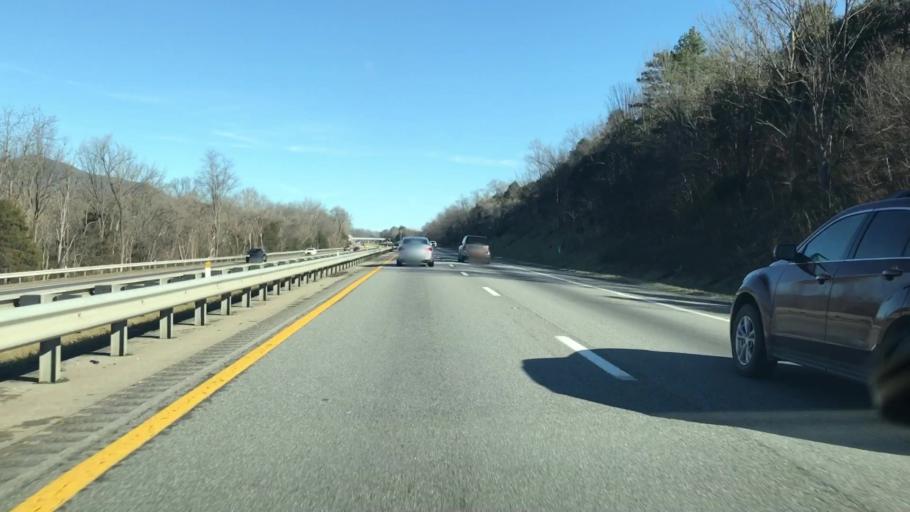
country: US
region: Virginia
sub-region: Botetourt County
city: Buchanan
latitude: 37.5669
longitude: -79.6517
